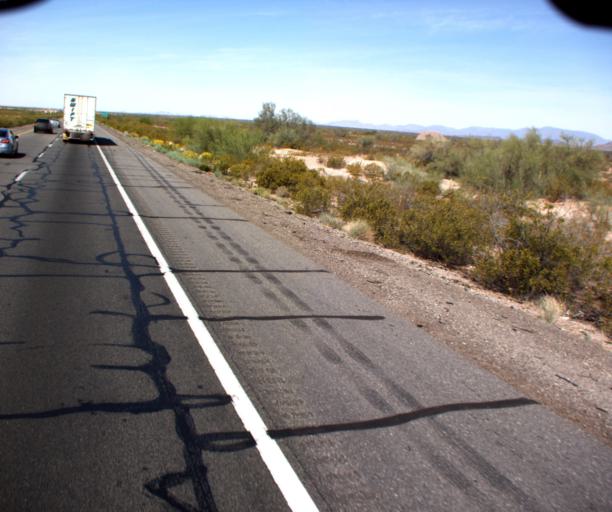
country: US
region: Arizona
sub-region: La Paz County
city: Salome
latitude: 33.5321
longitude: -113.1293
